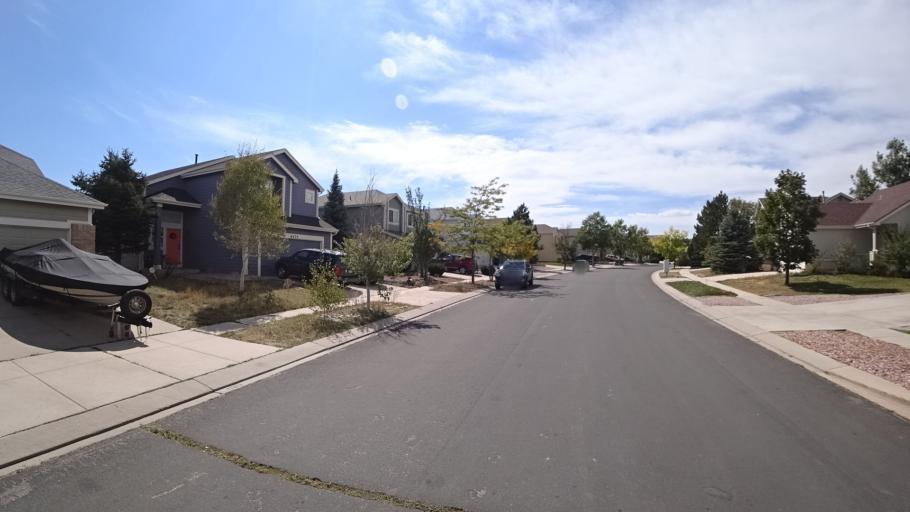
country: US
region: Colorado
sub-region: El Paso County
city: Cimarron Hills
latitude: 38.8980
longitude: -104.7126
